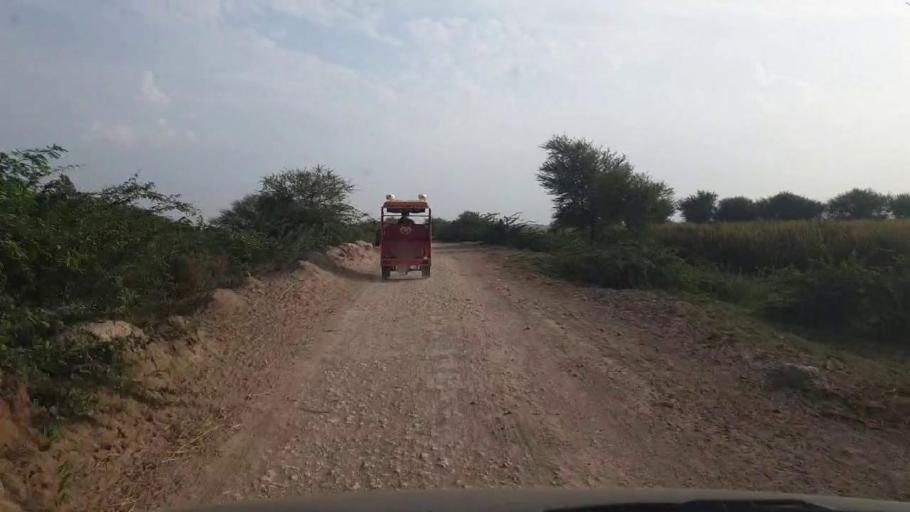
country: PK
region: Sindh
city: Badin
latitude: 24.5659
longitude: 68.6674
